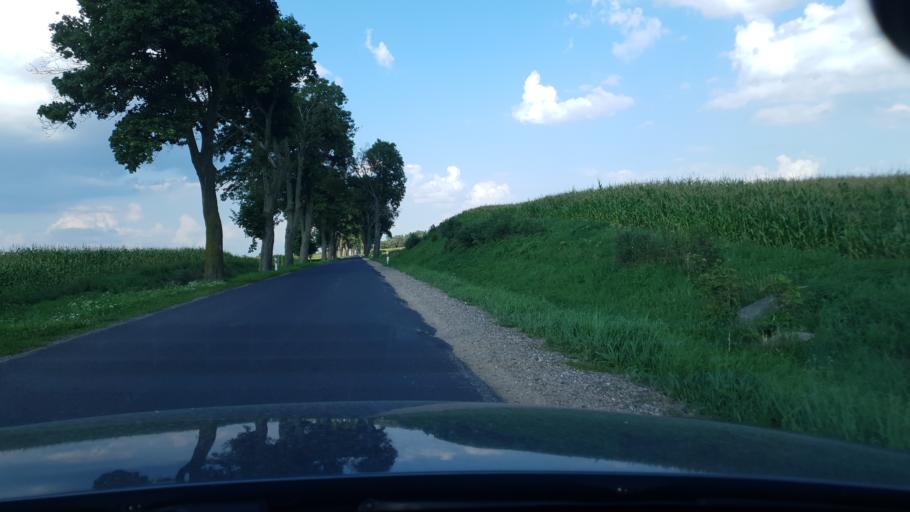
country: PL
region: Kujawsko-Pomorskie
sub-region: Powiat wabrzeski
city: Wabrzezno
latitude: 53.2569
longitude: 18.8885
